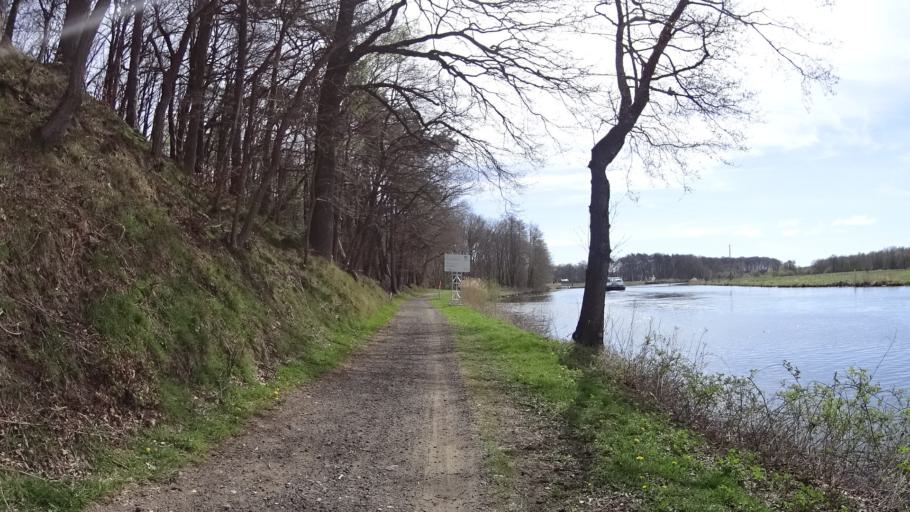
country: DE
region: Lower Saxony
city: Lingen
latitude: 52.4625
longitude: 7.3236
